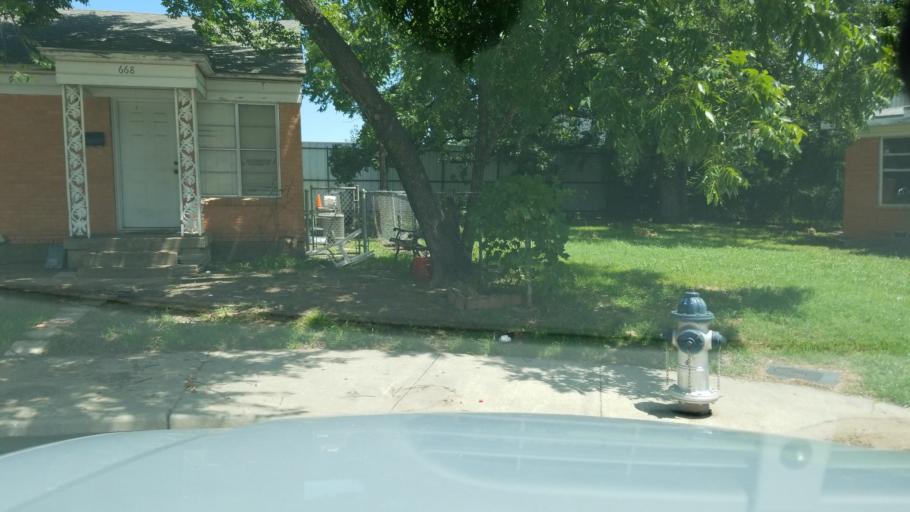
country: US
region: Texas
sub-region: Dallas County
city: Irving
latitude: 32.8060
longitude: -96.9279
